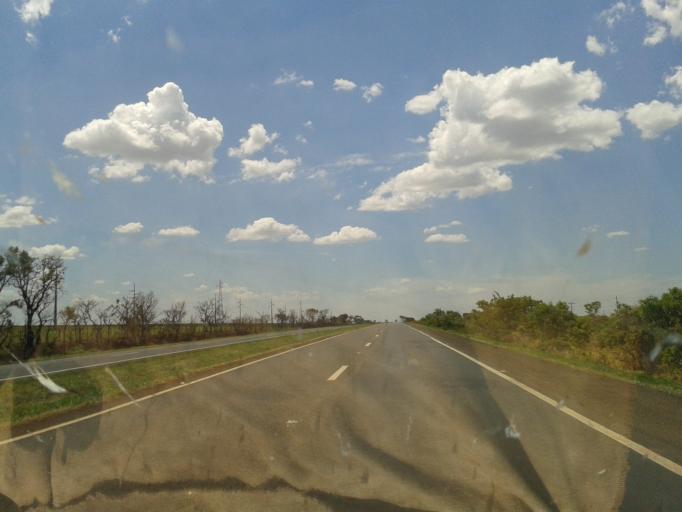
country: BR
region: Minas Gerais
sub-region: Uberlandia
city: Uberlandia
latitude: -19.0564
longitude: -48.1945
